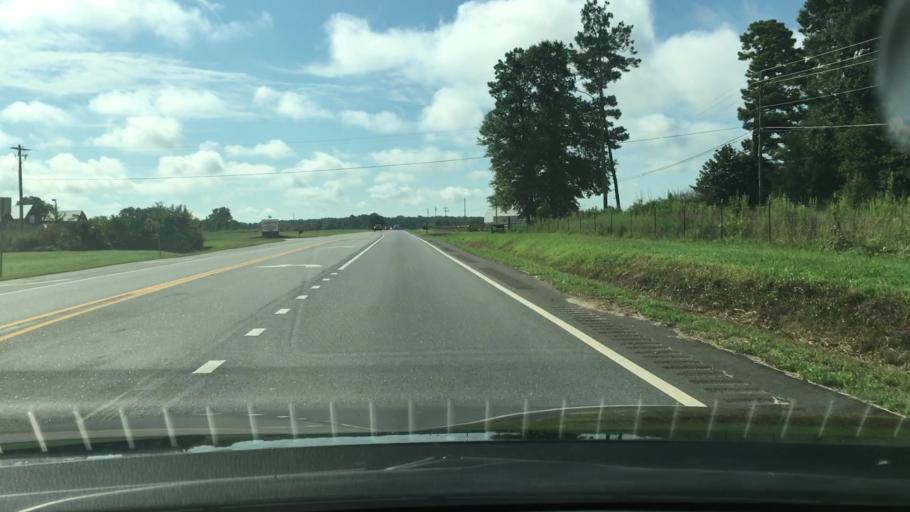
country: US
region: Georgia
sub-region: Morgan County
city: Madison
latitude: 33.5410
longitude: -83.4643
